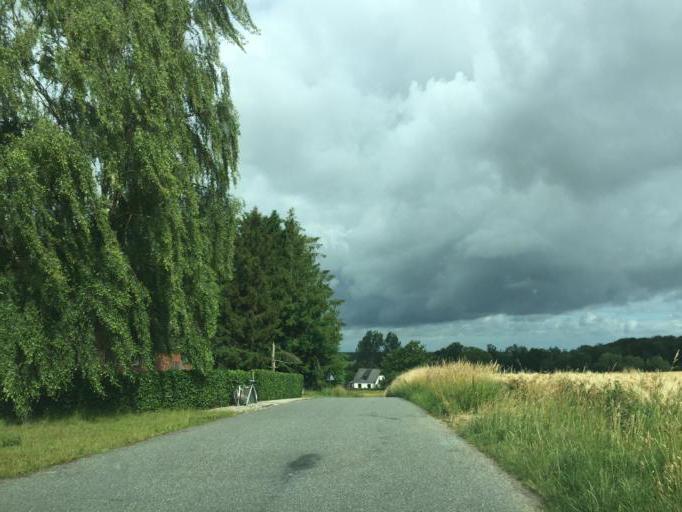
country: DK
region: South Denmark
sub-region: Faaborg-Midtfyn Kommune
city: Arslev
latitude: 55.2894
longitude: 10.4767
